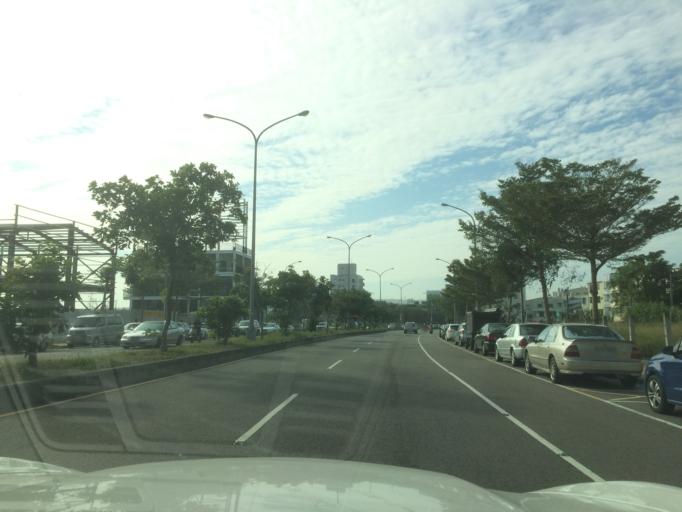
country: TW
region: Taiwan
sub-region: Taichung City
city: Taichung
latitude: 24.1509
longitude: 120.6326
